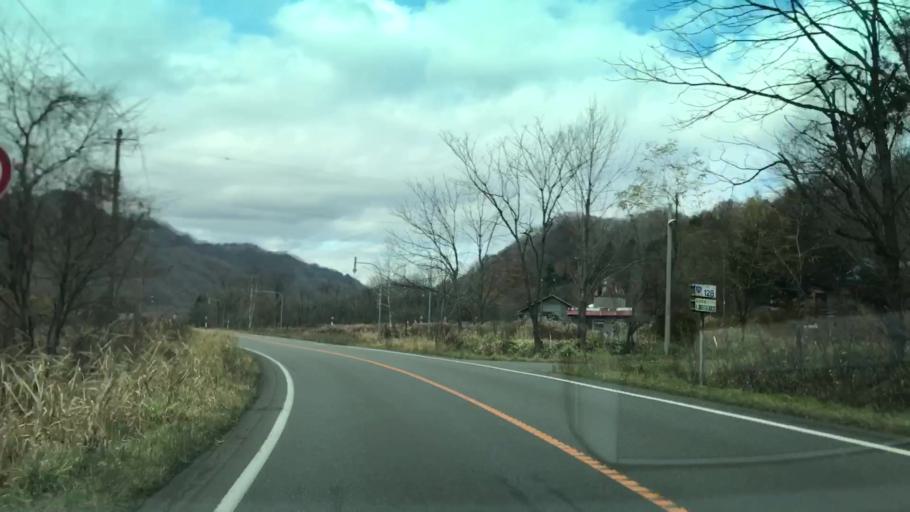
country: JP
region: Hokkaido
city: Shizunai-furukawacho
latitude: 42.8166
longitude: 142.4216
